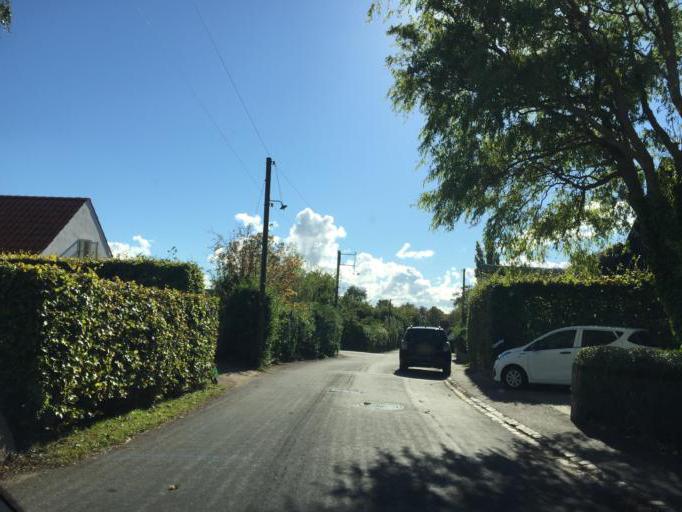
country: DK
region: Zealand
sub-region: Roskilde Kommune
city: Roskilde
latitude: 55.6781
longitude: 12.0877
